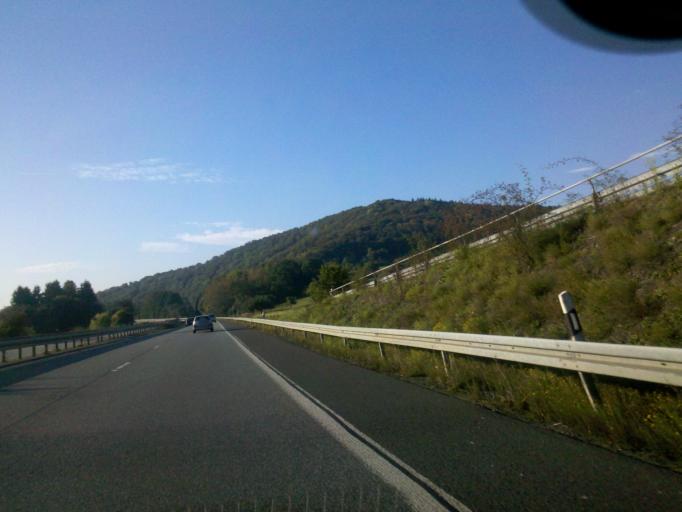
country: DE
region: Hesse
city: Herborn
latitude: 50.7131
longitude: 8.3050
